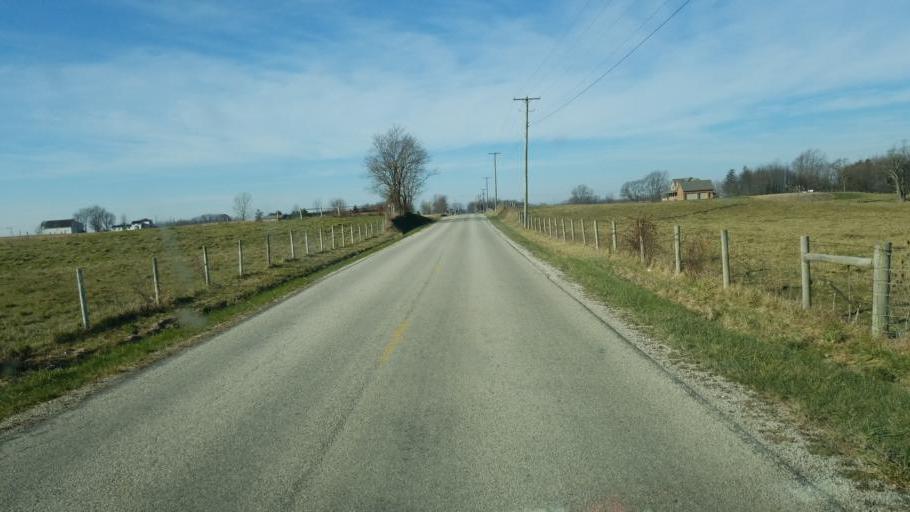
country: US
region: Ohio
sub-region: Richland County
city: Shelby
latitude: 40.8432
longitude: -82.6538
